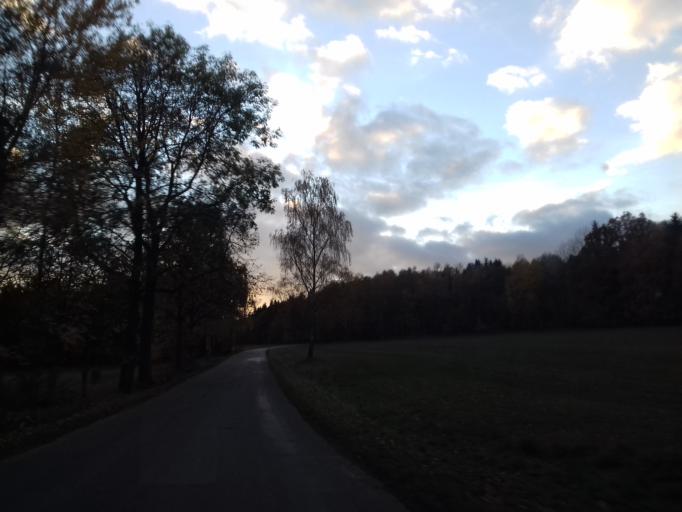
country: CZ
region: Pardubicky
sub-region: Okres Chrudim
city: Hlinsko
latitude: 49.7935
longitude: 15.9487
